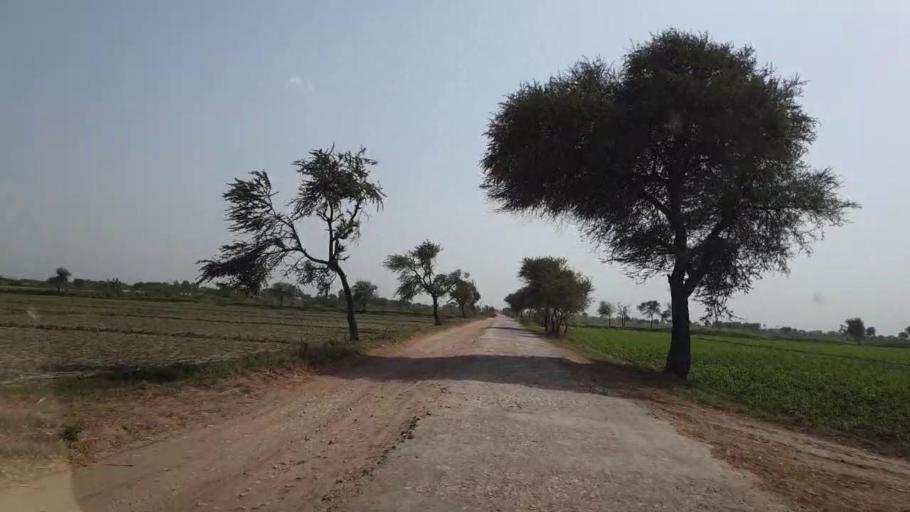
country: PK
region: Sindh
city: Rajo Khanani
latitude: 25.0284
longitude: 68.8730
